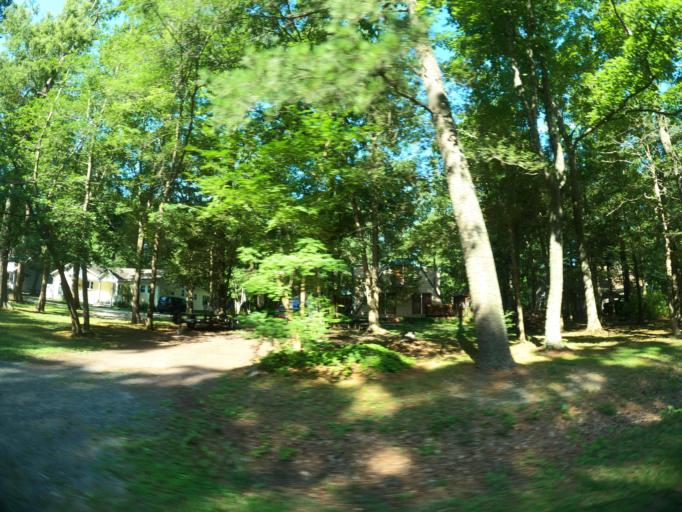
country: US
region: Delaware
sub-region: Sussex County
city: Ocean View
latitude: 38.4741
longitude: -75.1154
